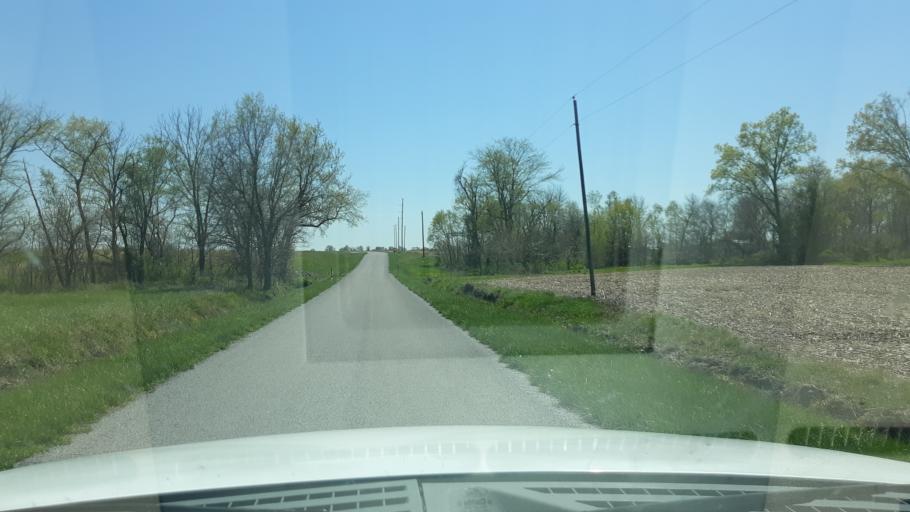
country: US
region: Illinois
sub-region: Saline County
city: Harrisburg
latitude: 37.8872
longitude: -88.6699
